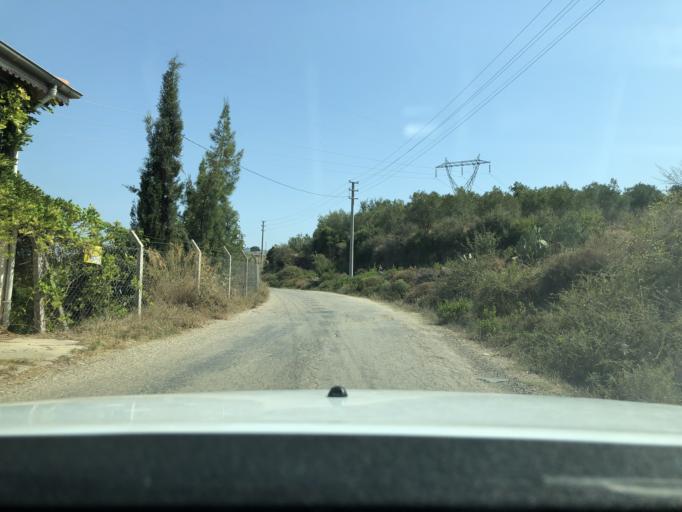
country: TR
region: Antalya
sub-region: Manavgat
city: Manavgat
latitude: 36.8021
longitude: 31.4696
